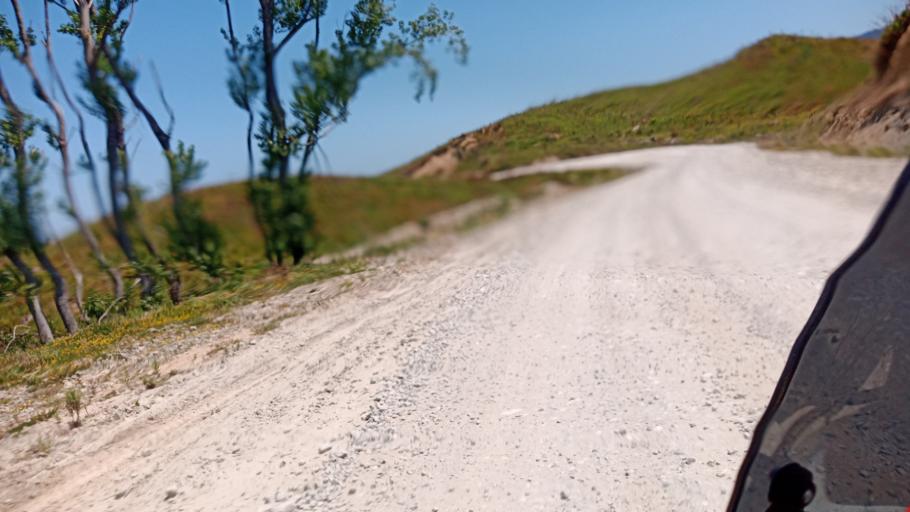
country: NZ
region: Gisborne
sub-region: Gisborne District
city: Gisborne
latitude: -38.2898
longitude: 178.0132
